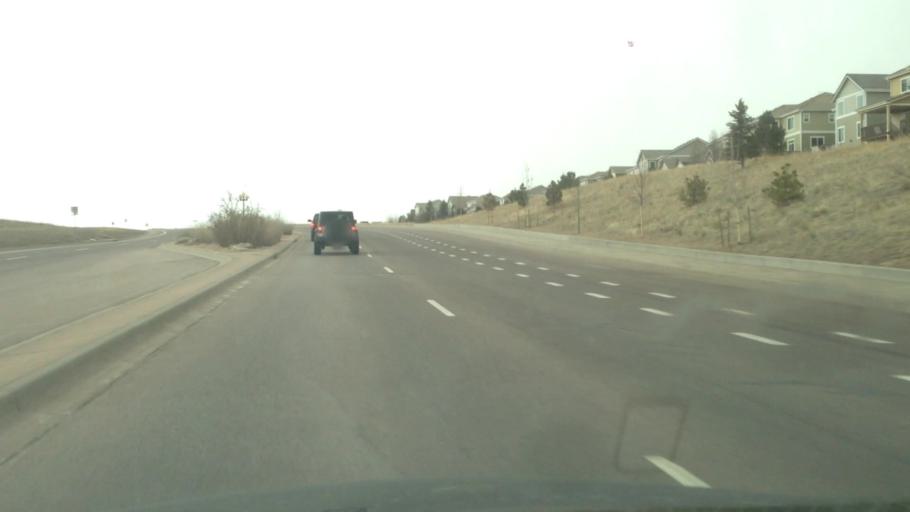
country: US
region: Colorado
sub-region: Douglas County
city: Stonegate
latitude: 39.4930
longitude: -104.8029
